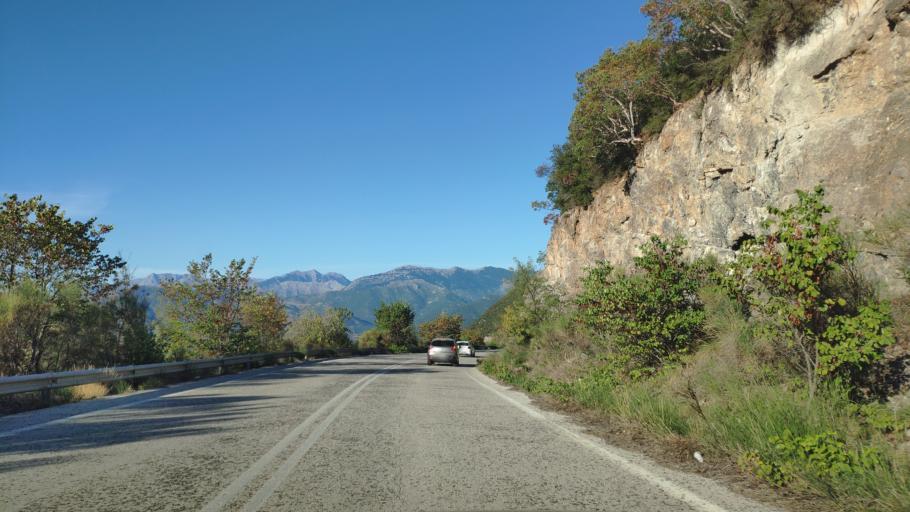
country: GR
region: Peloponnese
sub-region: Nomos Arkadias
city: Langadhia
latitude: 37.7110
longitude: 22.1958
